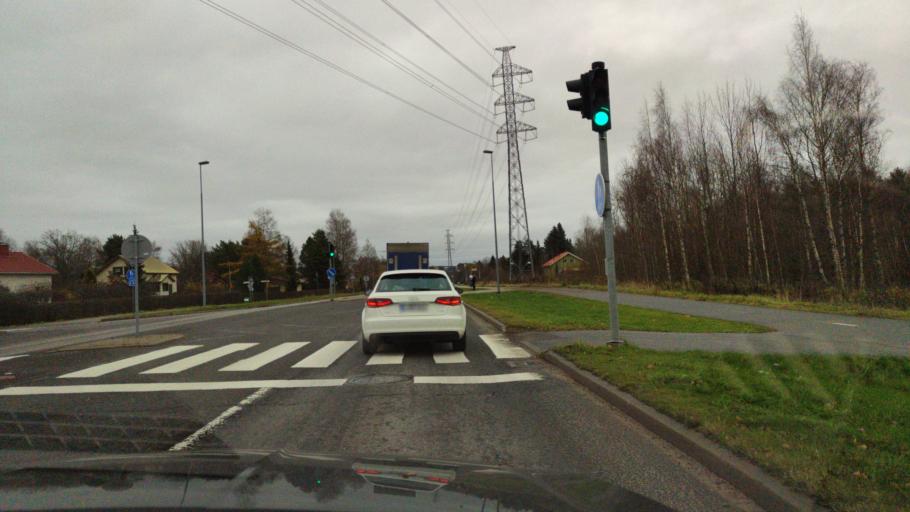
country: FI
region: Varsinais-Suomi
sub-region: Turku
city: Turku
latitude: 60.4764
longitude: 22.2597
